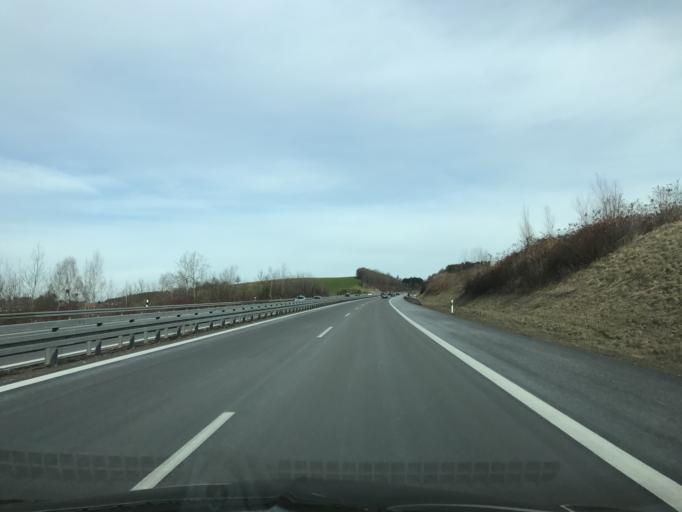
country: DE
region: Bavaria
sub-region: Swabia
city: Weissensberg
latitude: 47.6012
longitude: 9.7322
